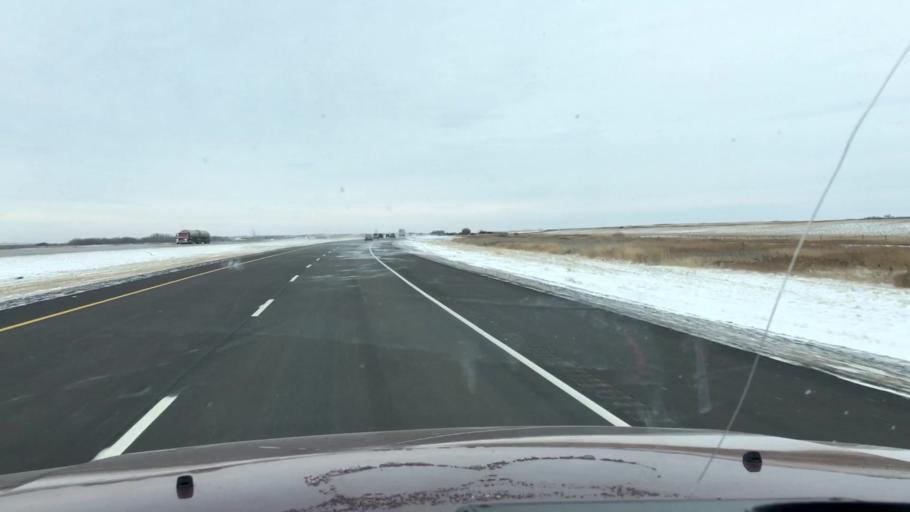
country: CA
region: Saskatchewan
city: Moose Jaw
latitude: 50.8979
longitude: -105.6316
